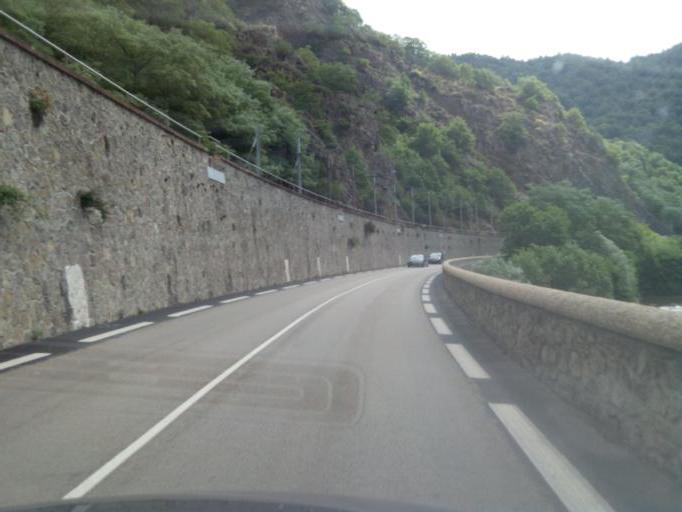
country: FR
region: Auvergne
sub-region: Departement de la Haute-Loire
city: Chadrac
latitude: 45.0933
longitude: 3.9082
